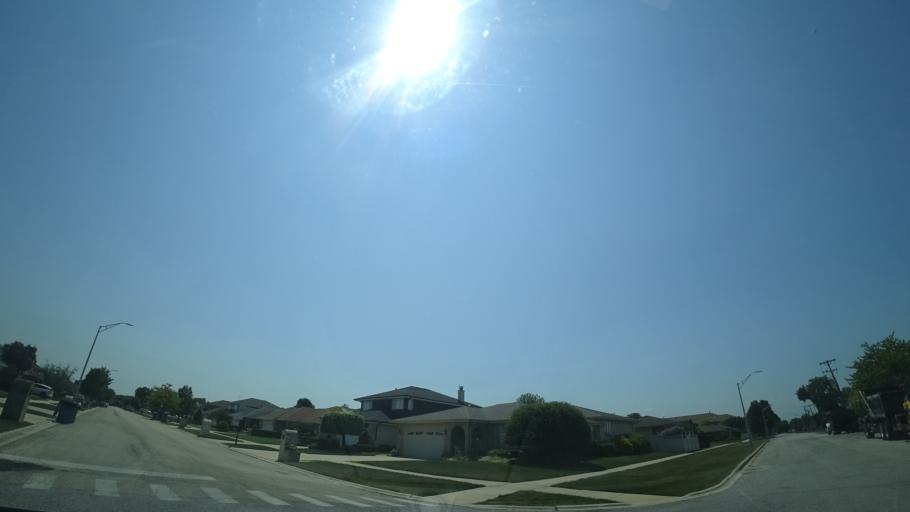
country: US
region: Illinois
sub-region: Cook County
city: Oak Lawn
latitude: 41.6979
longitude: -87.7562
